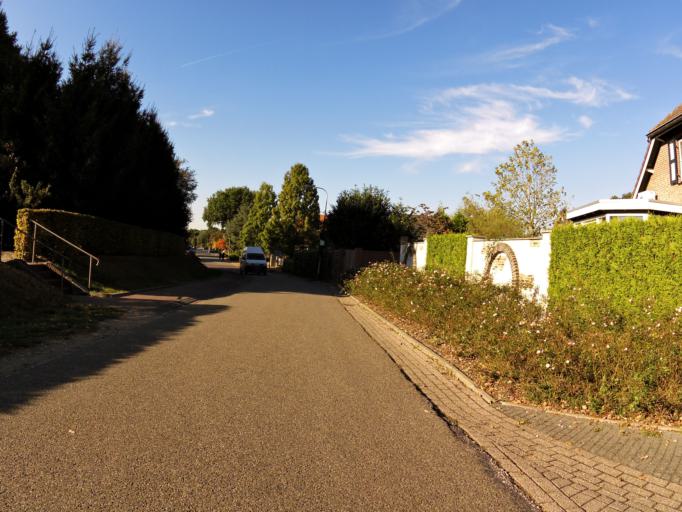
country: NL
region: Limburg
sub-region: Gemeente Bergen
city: Wellerlooi
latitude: 51.5344
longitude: 6.1377
